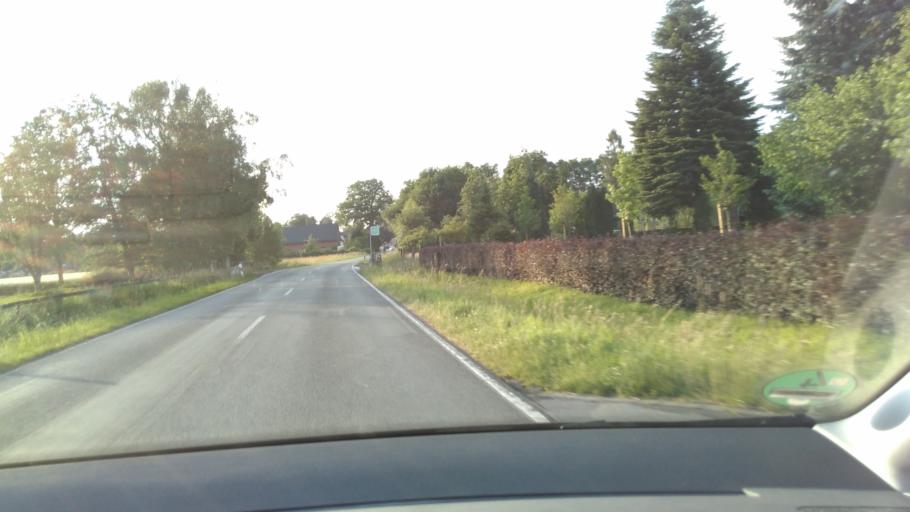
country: DE
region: North Rhine-Westphalia
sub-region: Regierungsbezirk Detmold
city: Verl
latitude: 51.8617
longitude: 8.4996
